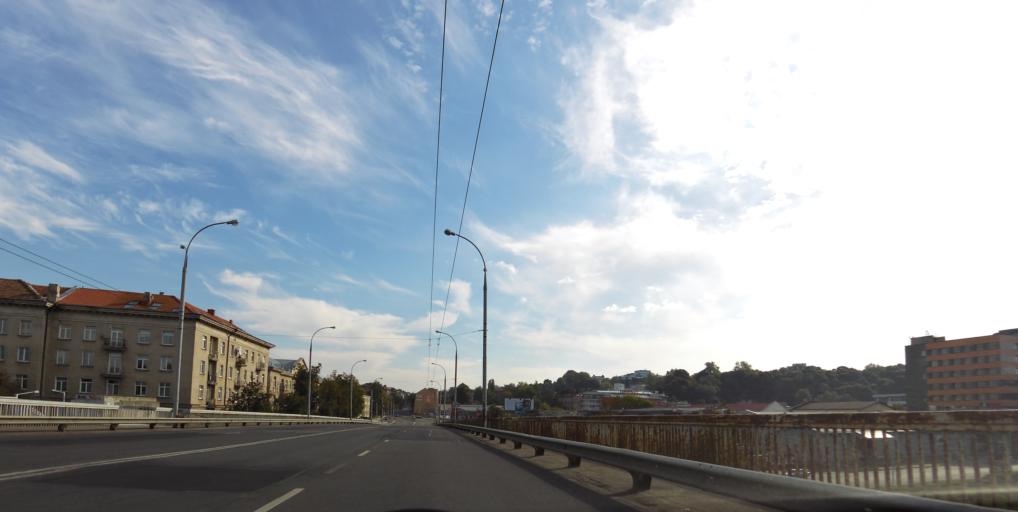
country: LT
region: Vilnius County
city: Naujamiestis
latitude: 54.6888
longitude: 25.2586
